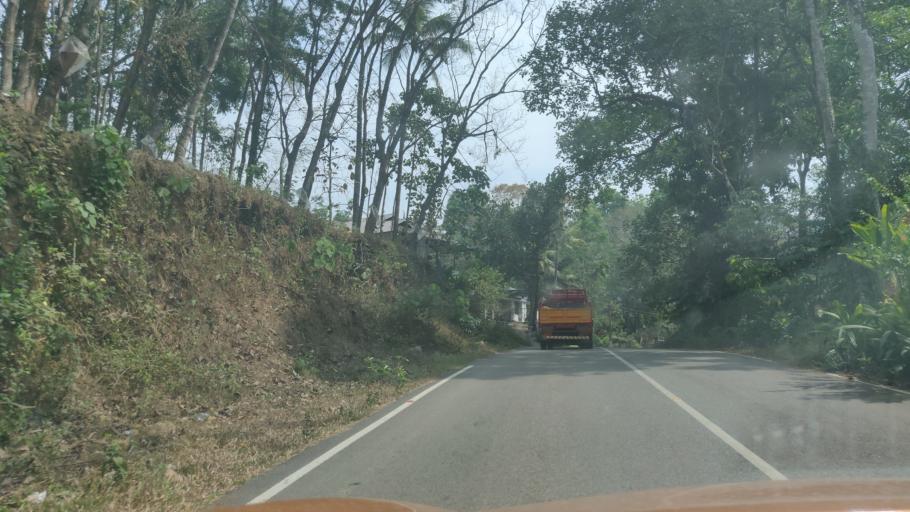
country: IN
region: Kerala
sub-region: Ernakulam
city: Muvattupuzha
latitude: 9.8856
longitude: 76.6536
